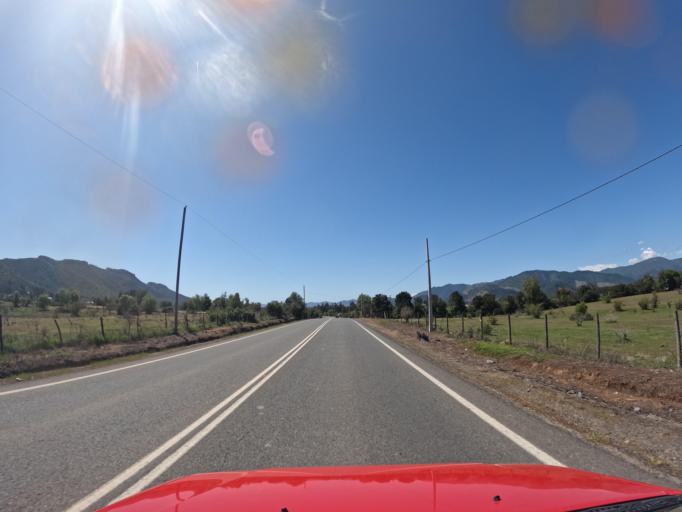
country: CL
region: Maule
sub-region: Provincia de Talca
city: San Clemente
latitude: -35.4403
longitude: -71.2641
